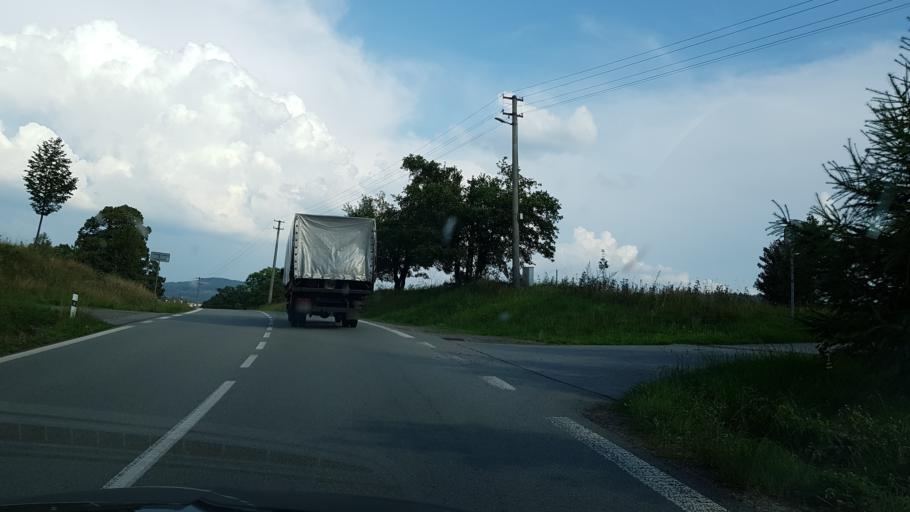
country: CZ
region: Pardubicky
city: Jablonne nad Orlici
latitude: 50.0915
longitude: 16.5811
